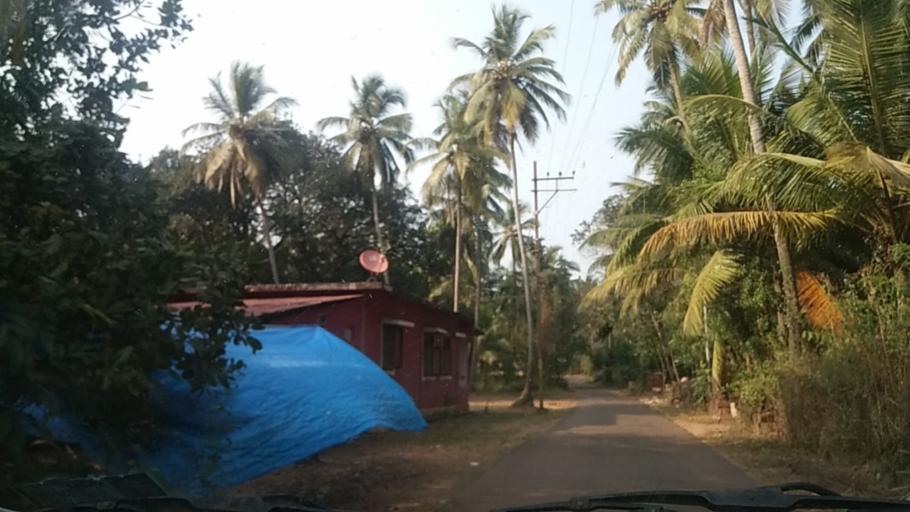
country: IN
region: Goa
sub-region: South Goa
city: Colva
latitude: 15.3187
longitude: 73.9322
